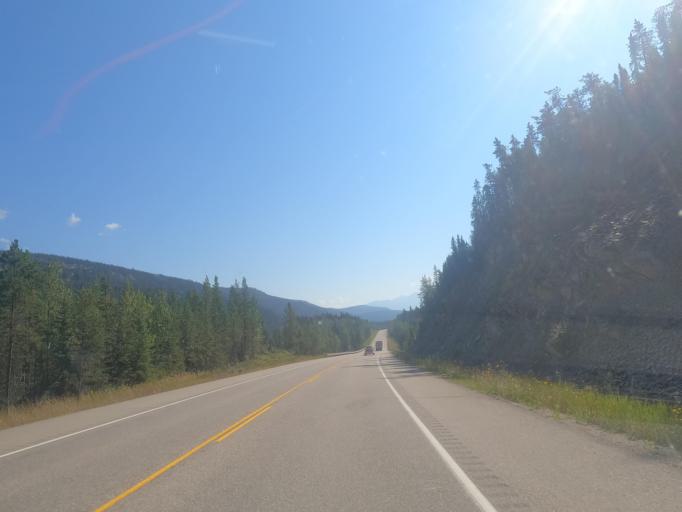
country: CA
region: Alberta
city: Jasper Park Lodge
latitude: 52.8769
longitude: -118.3318
